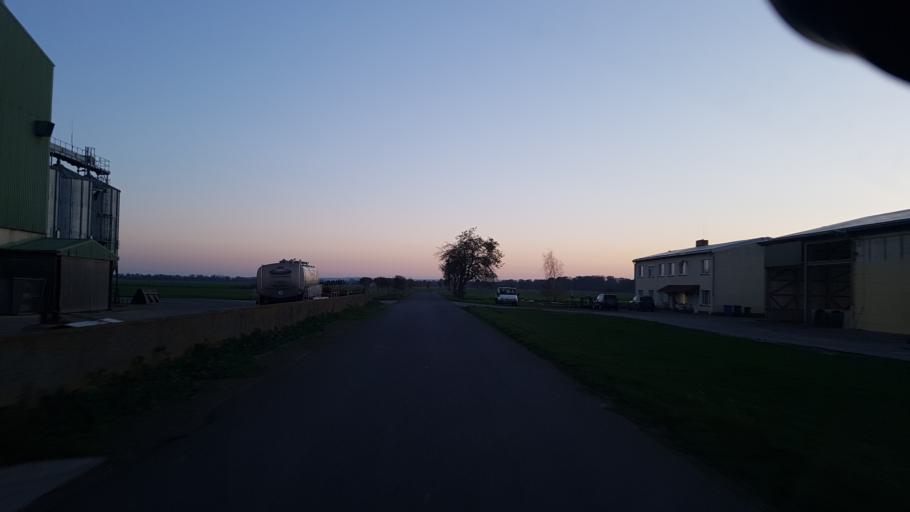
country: DE
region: Saxony
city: Beilrode
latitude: 51.5604
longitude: 13.0623
